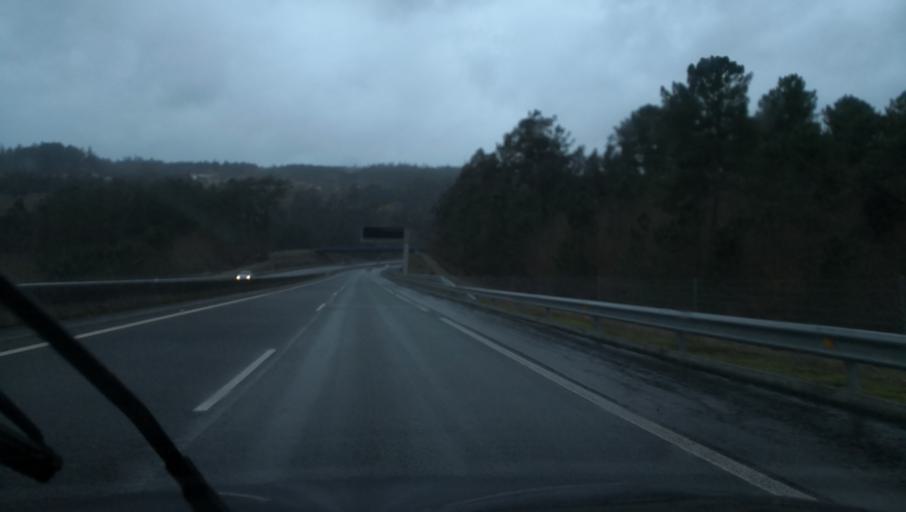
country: ES
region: Galicia
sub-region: Provincia da Coruna
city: Santiago de Compostela
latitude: 42.8266
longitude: -8.5187
